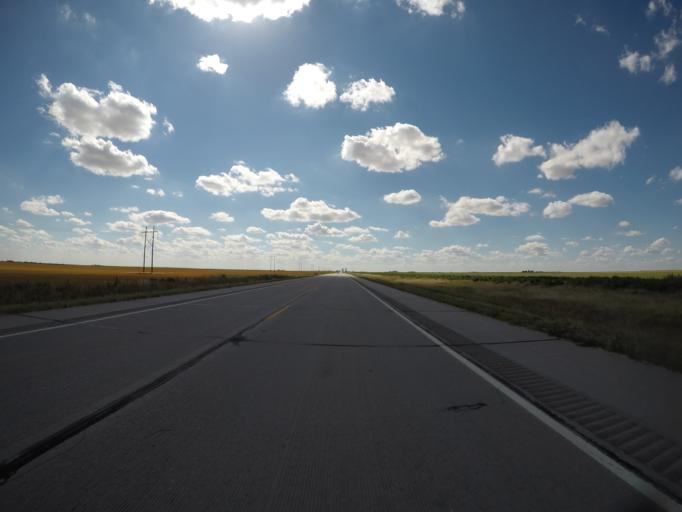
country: US
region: Colorado
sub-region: Phillips County
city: Holyoke
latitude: 40.6045
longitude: -102.4239
